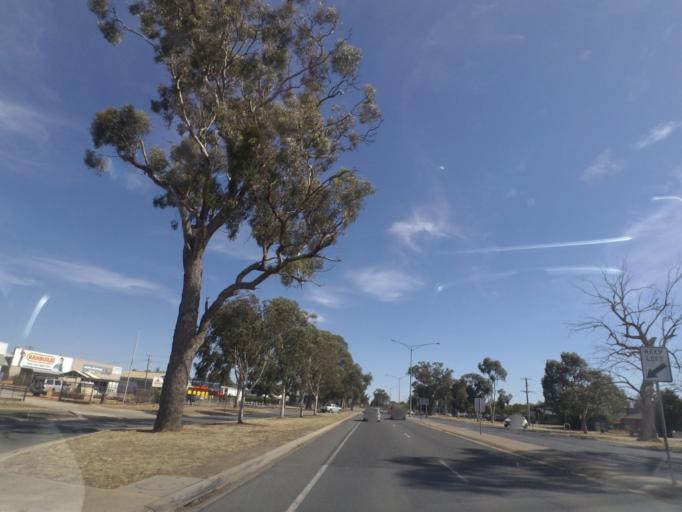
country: AU
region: Victoria
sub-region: Greater Shepparton
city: Shepparton
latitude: -36.4116
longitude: 145.3929
